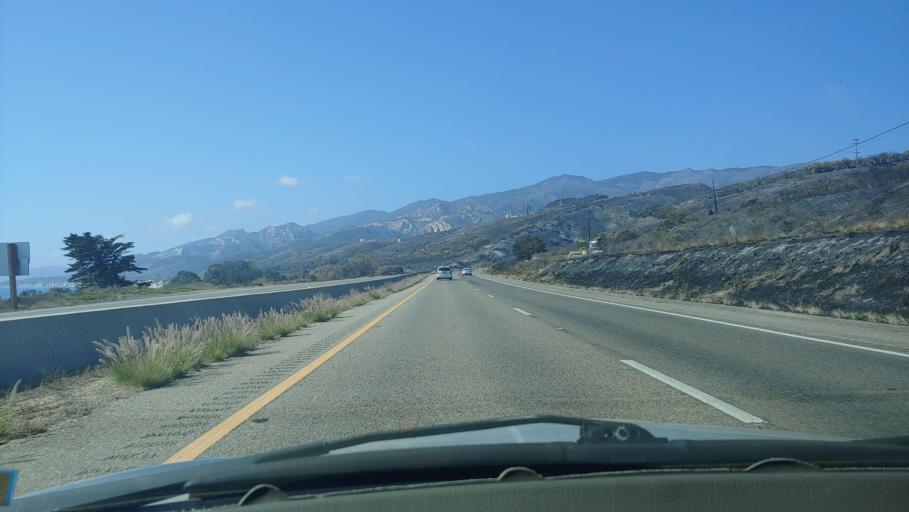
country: US
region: California
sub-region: Santa Barbara County
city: Solvang
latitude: 34.4692
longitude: -120.1121
